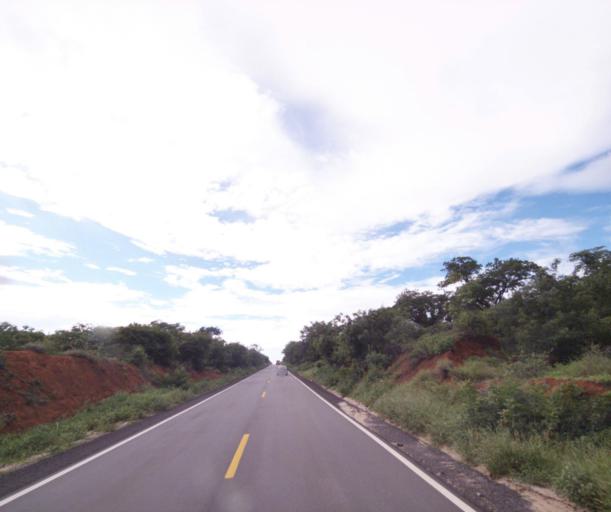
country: BR
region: Bahia
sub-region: Guanambi
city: Guanambi
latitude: -14.3949
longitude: -42.7551
